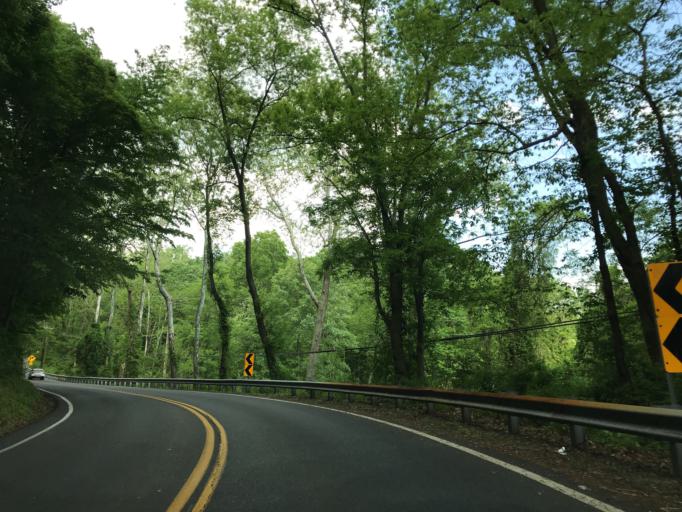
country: US
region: Maryland
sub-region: Harford County
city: North Bel Air
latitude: 39.5247
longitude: -76.3673
